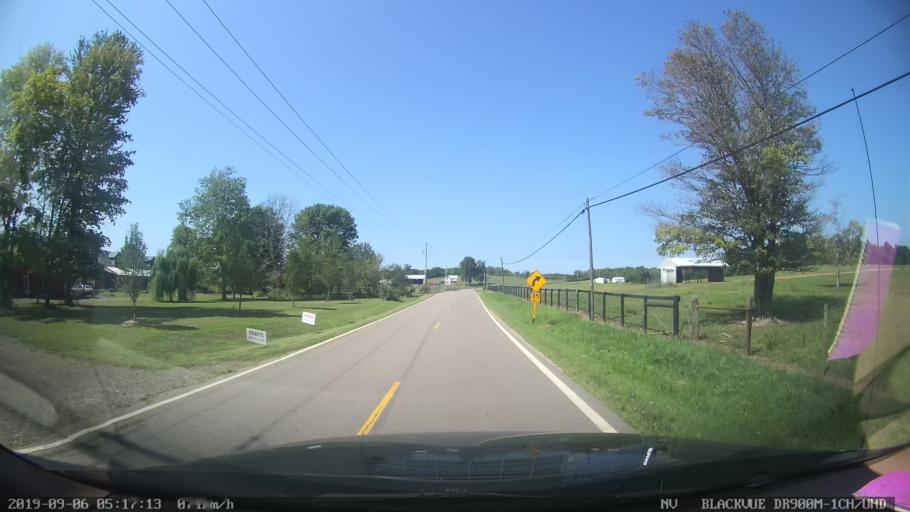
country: US
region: Ohio
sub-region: Licking County
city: Utica
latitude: 40.2026
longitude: -82.3606
